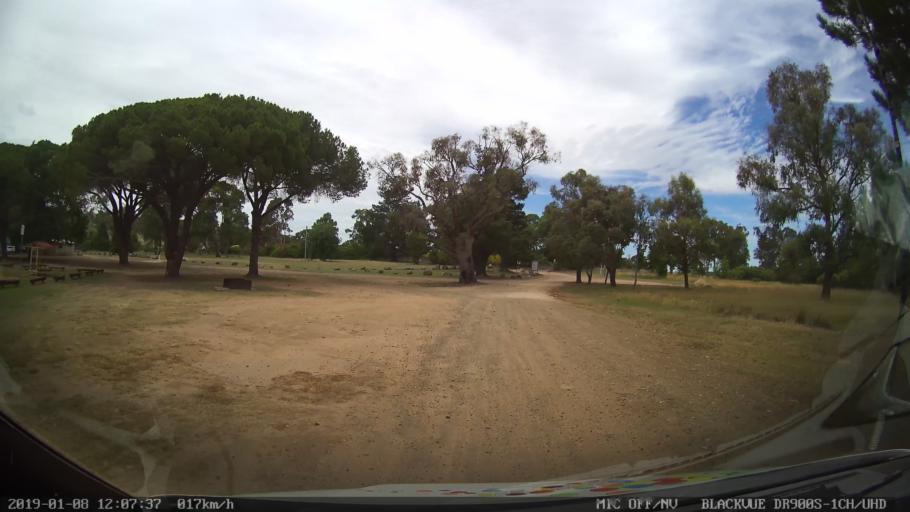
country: AU
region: New South Wales
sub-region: Armidale Dumaresq
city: Armidale
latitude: -30.4289
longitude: 151.5943
